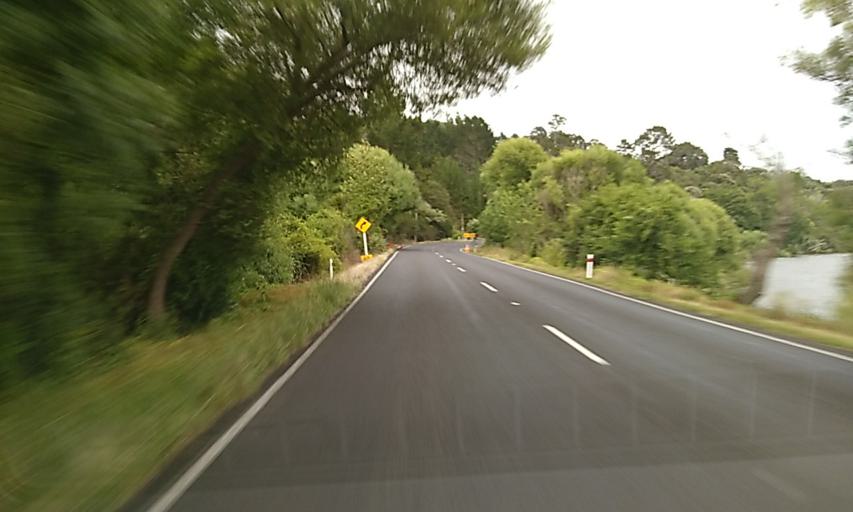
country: NZ
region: Auckland
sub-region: Auckland
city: Pukekohe East
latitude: -37.3021
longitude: 174.9474
